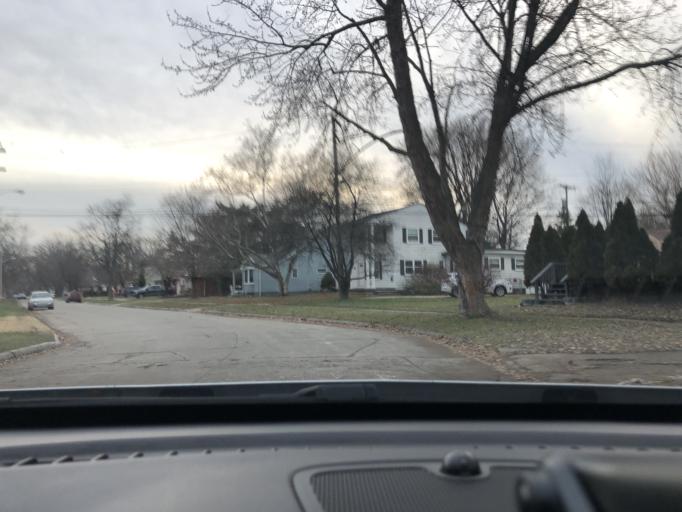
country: US
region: Michigan
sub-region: Wayne County
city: Allen Park
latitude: 42.2792
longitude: -83.2229
